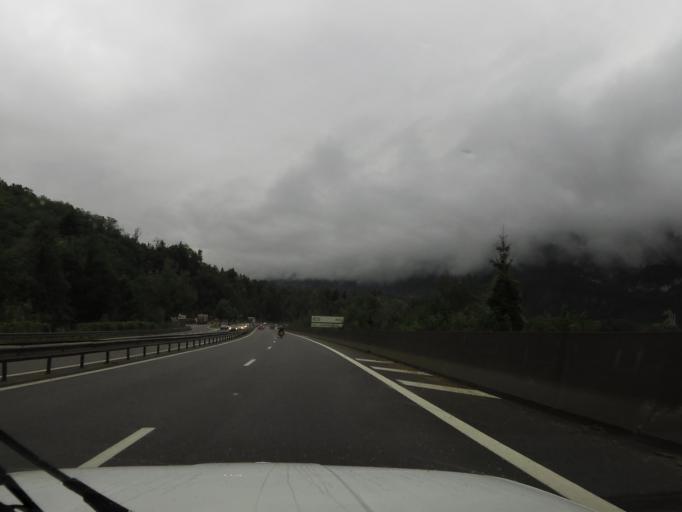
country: FR
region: Rhone-Alpes
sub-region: Departement de la Savoie
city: Novalaise
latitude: 45.5707
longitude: 5.7917
